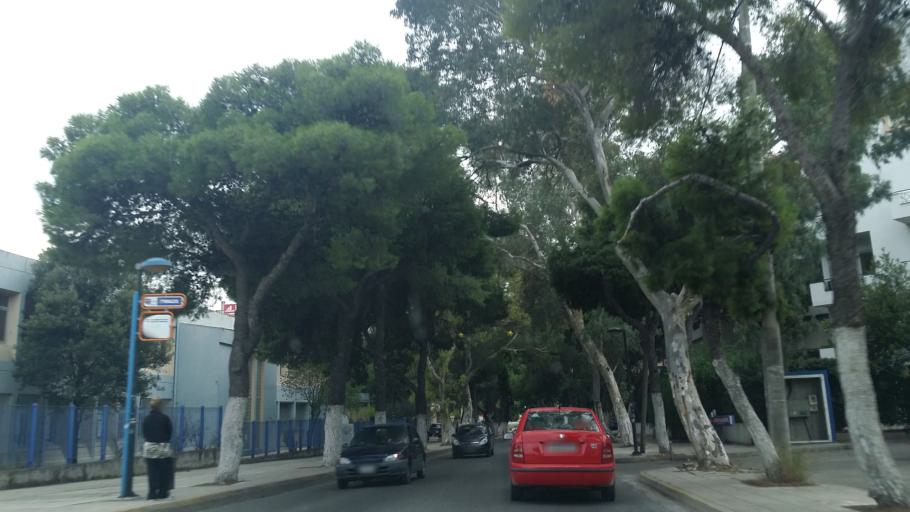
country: GR
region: Attica
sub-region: Nomarchia Athinas
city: Metamorfosi
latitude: 38.0651
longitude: 23.7593
